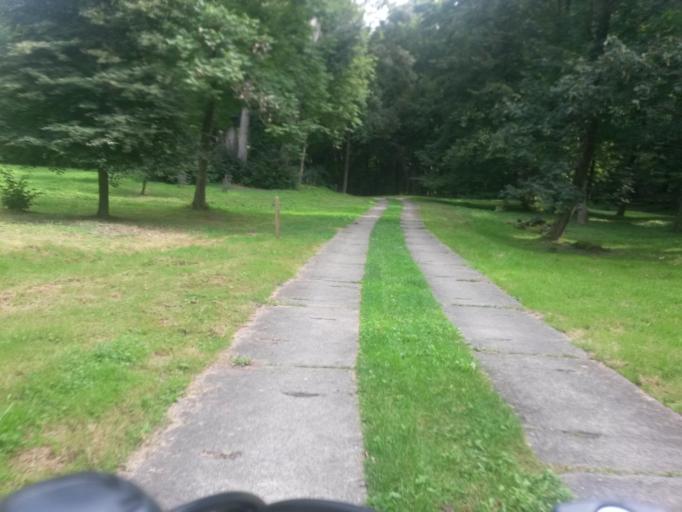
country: DE
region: Brandenburg
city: Angermunde
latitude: 53.0564
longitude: 13.9539
